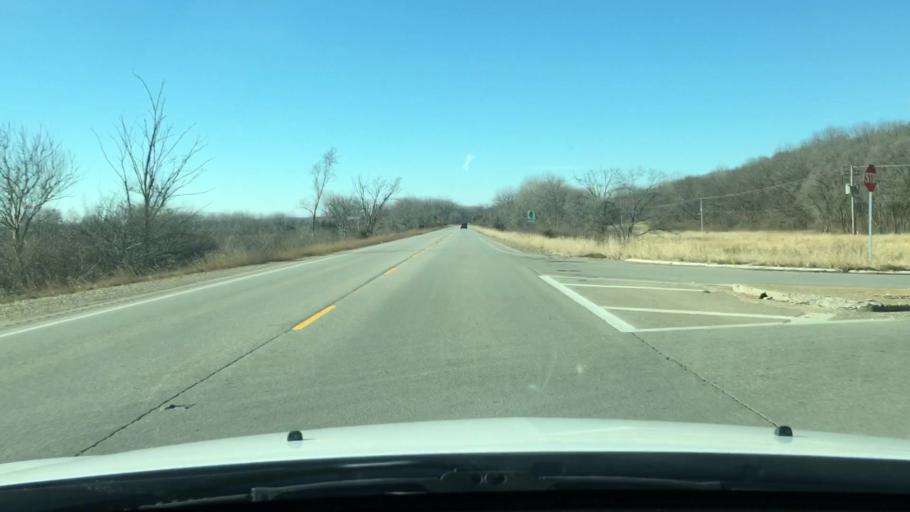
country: US
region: Illinois
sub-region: Peoria County
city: Glasford
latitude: 40.5516
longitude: -89.8051
